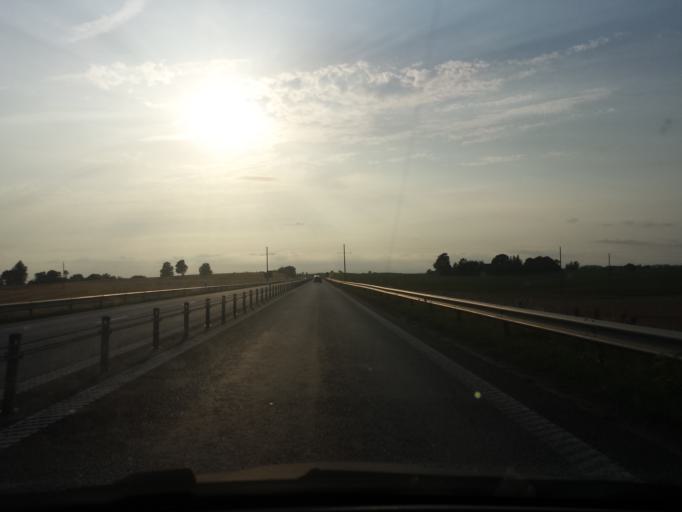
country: SE
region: Skane
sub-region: Skurups Kommun
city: Rydsgard
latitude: 55.4793
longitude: 13.6263
